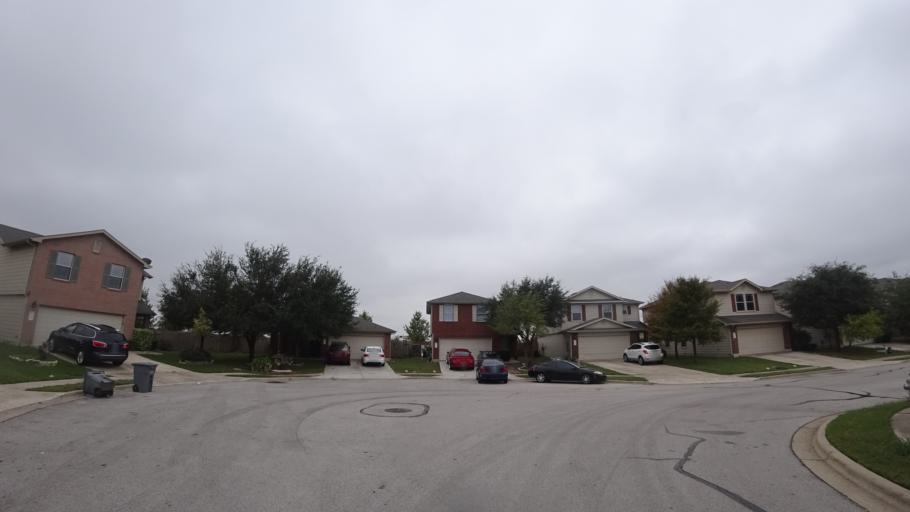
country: US
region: Texas
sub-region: Travis County
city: Manor
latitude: 30.3709
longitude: -97.6132
